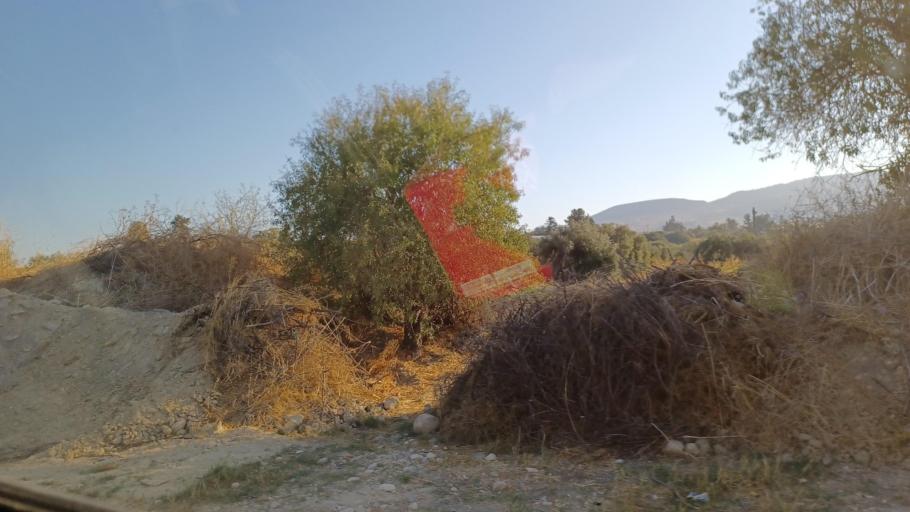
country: CY
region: Pafos
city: Polis
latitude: 35.0013
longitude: 32.4357
